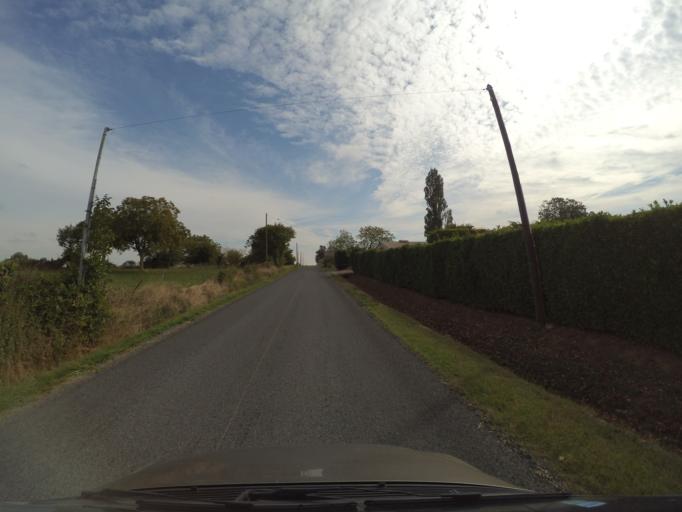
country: FR
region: Pays de la Loire
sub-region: Departement de Maine-et-Loire
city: Martigne-Briand
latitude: 47.2043
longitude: -0.4496
